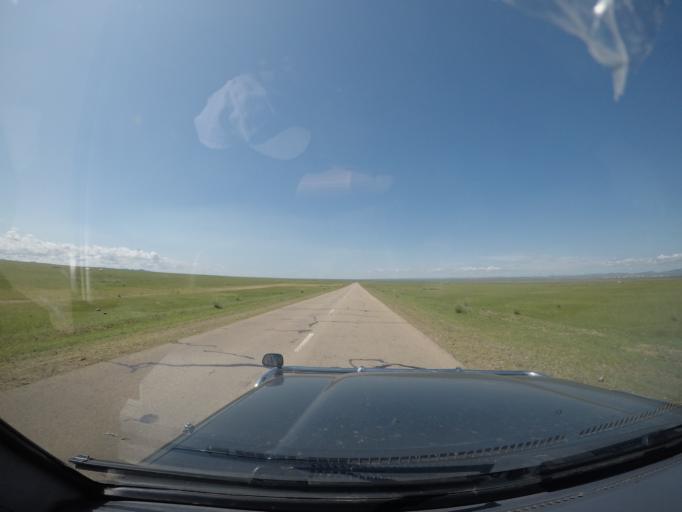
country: MN
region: Hentiy
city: Undurkhaan
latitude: 47.2789
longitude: 110.7522
